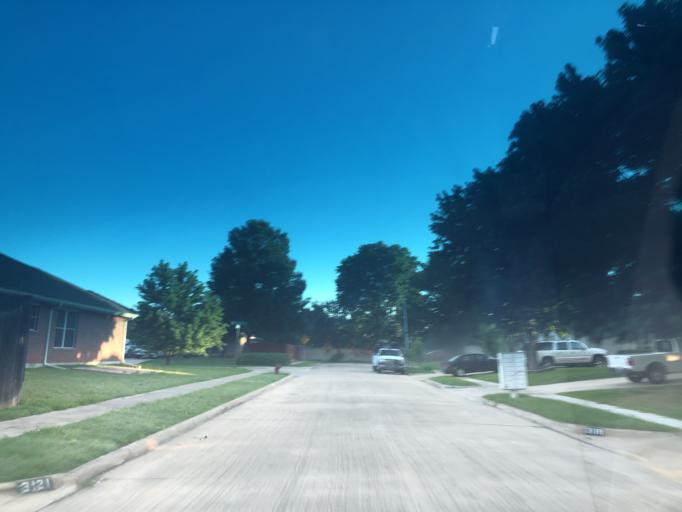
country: US
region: Texas
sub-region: Dallas County
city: Grand Prairie
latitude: 32.6955
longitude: -97.0137
